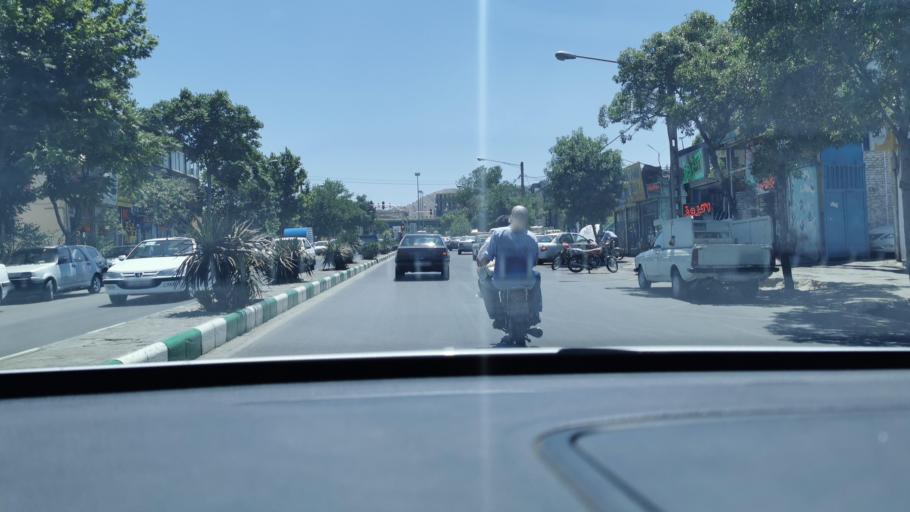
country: IR
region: Razavi Khorasan
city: Mashhad
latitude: 36.2587
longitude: 59.6012
